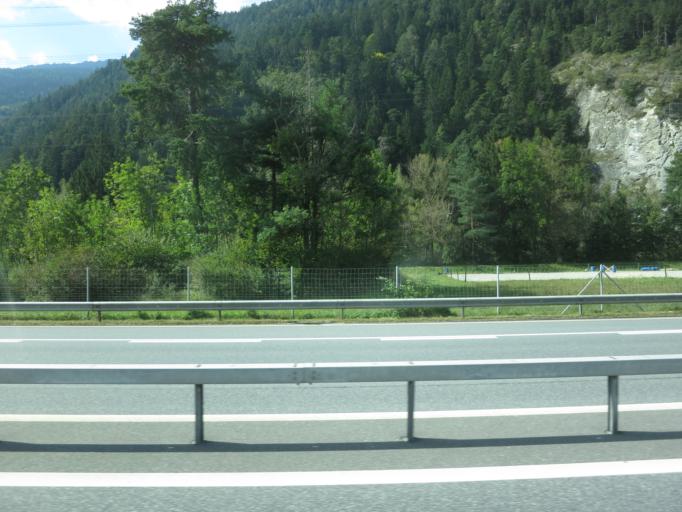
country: CH
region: Grisons
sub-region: Imboden District
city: Rhazuns
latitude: 46.7686
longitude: 9.4215
